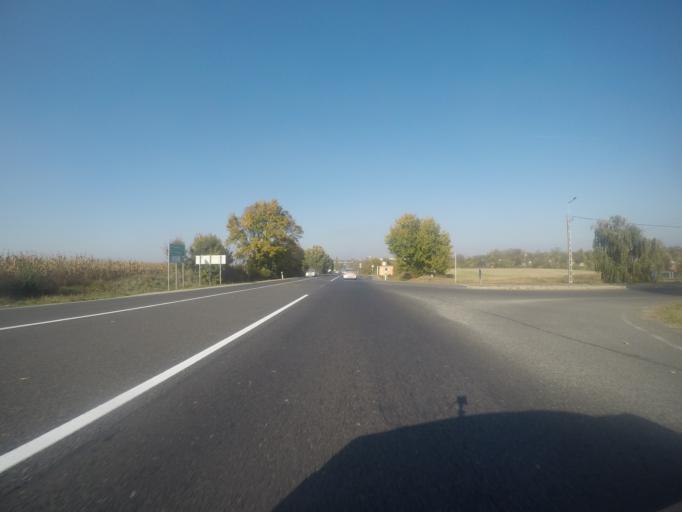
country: HU
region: Fejer
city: Baracs
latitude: 46.9004
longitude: 18.9235
